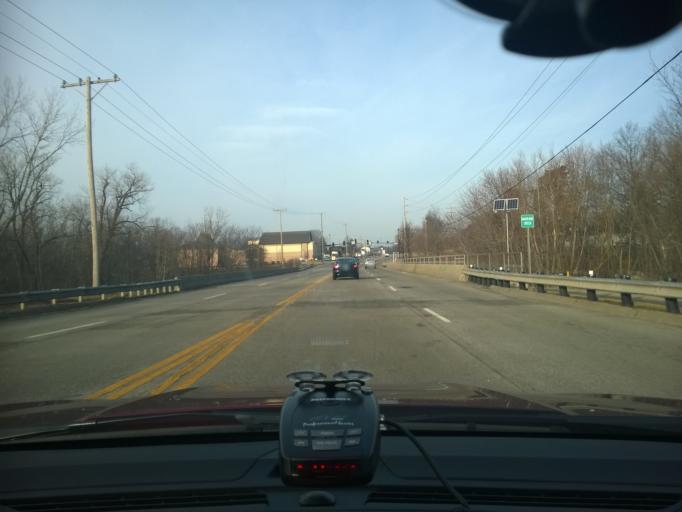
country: US
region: Missouri
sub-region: Saint Charles County
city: Saint Peters
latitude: 38.7874
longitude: -90.6448
